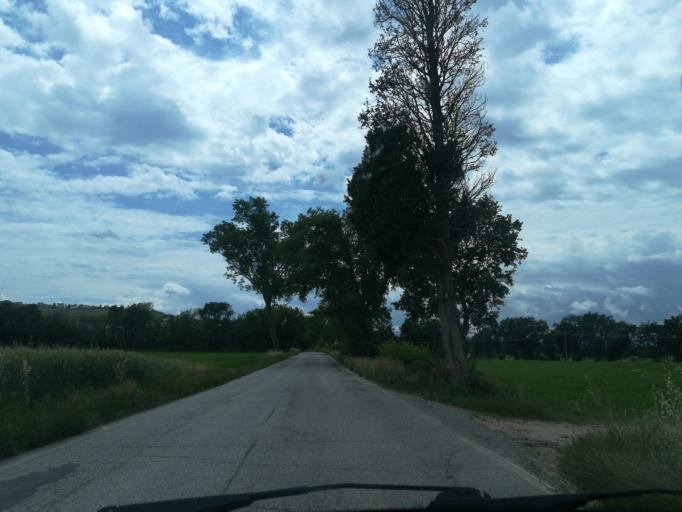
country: IT
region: The Marches
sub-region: Provincia di Macerata
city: Petriolo
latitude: 43.2386
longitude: 13.4711
